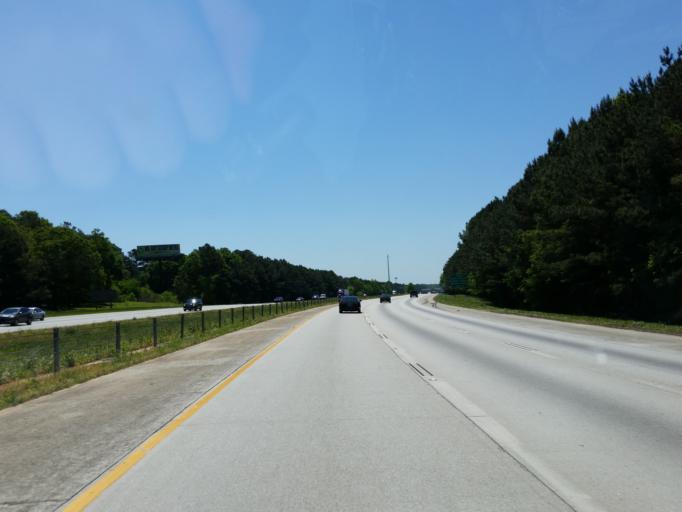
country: US
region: Georgia
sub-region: Clayton County
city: Conley
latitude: 33.6272
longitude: -84.2992
